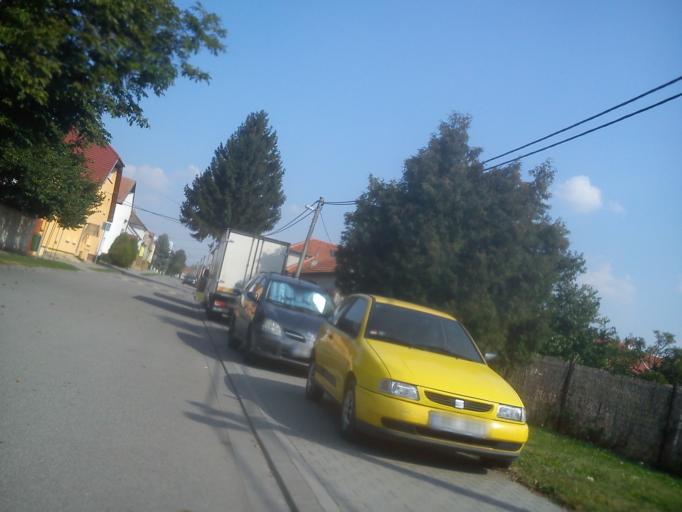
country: CZ
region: South Moravian
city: Sokolnice
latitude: 49.1030
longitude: 16.7493
